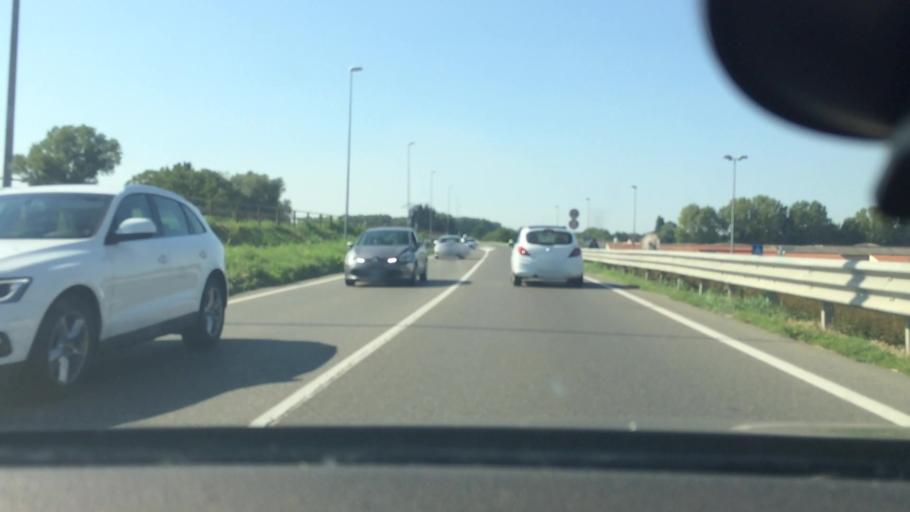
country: IT
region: Lombardy
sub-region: Provincia di Lodi
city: San Rocco al Porto
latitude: 45.0822
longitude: 9.6922
